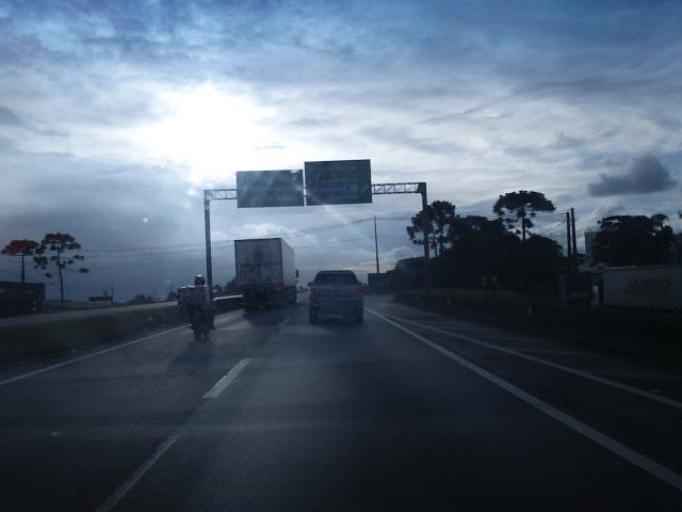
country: BR
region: Parana
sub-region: Sao Jose Dos Pinhais
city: Sao Jose dos Pinhais
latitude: -25.5678
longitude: -49.1745
